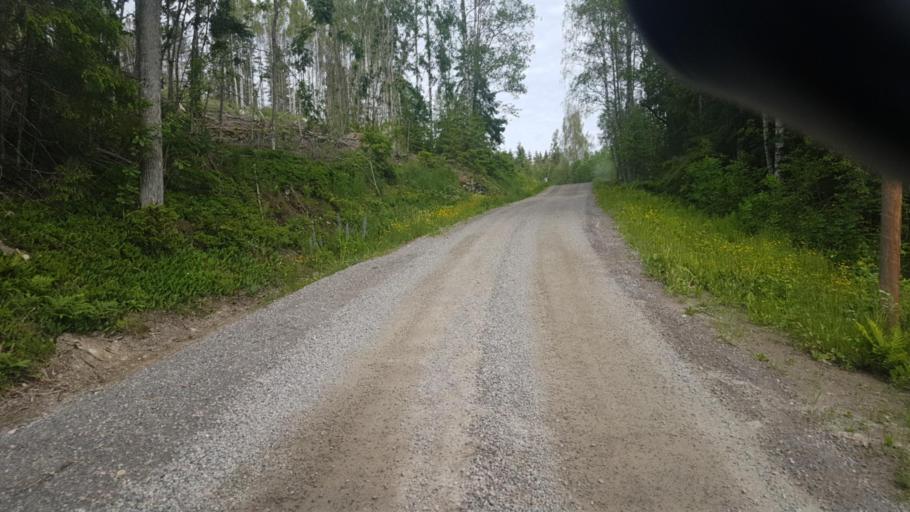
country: SE
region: Vaermland
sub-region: Eda Kommun
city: Amotfors
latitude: 59.8059
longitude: 12.4167
